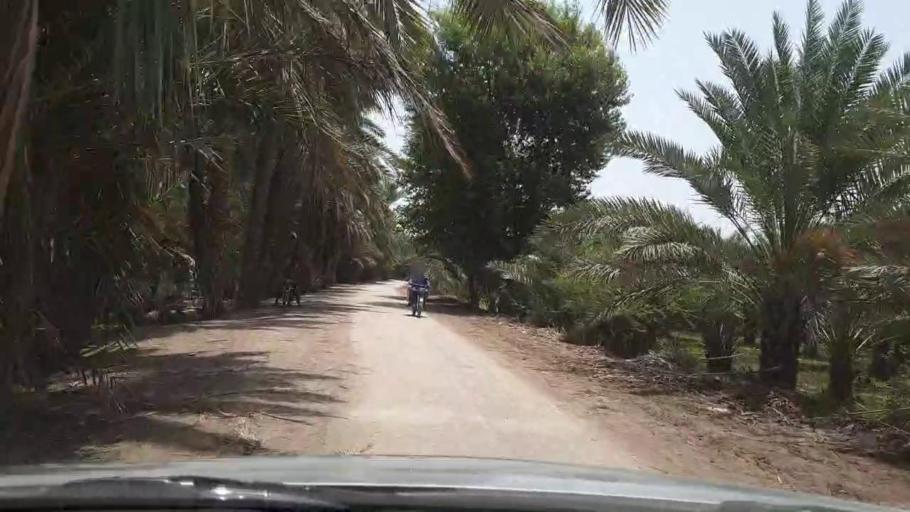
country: PK
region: Sindh
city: Pano Aqil
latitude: 27.8611
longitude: 69.0663
